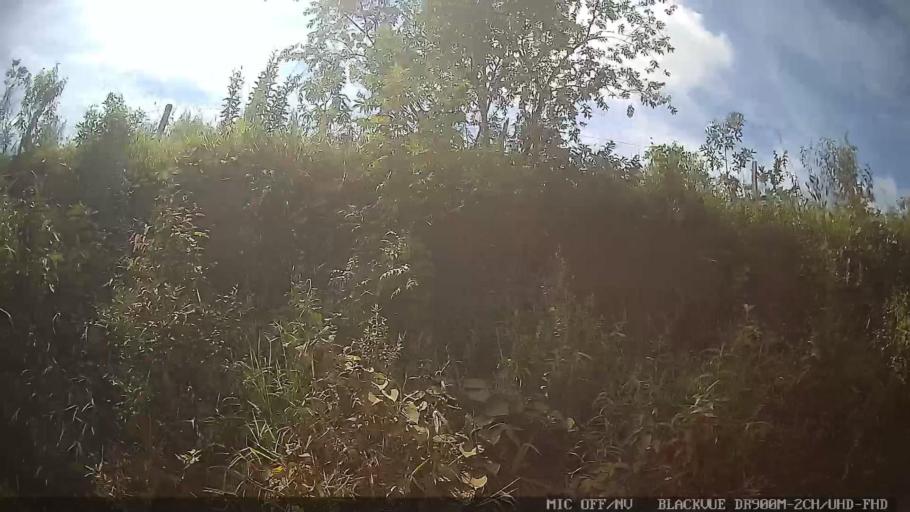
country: BR
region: Sao Paulo
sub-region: Braganca Paulista
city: Braganca Paulista
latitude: -22.9829
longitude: -46.6440
